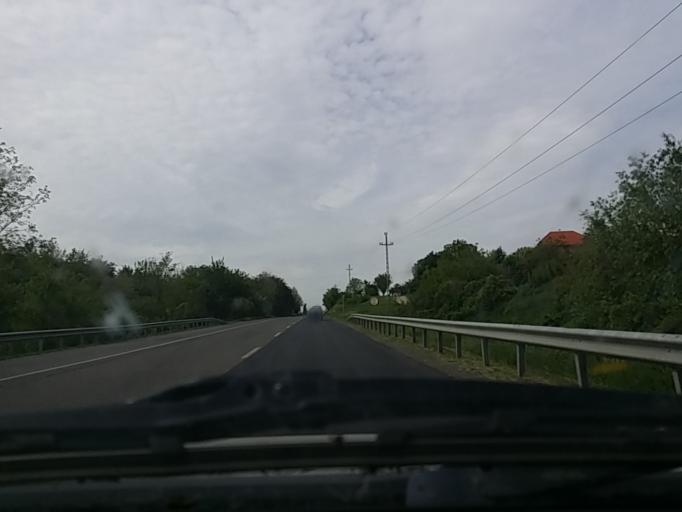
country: HU
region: Baranya
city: Harkany
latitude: 45.8859
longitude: 18.2368
